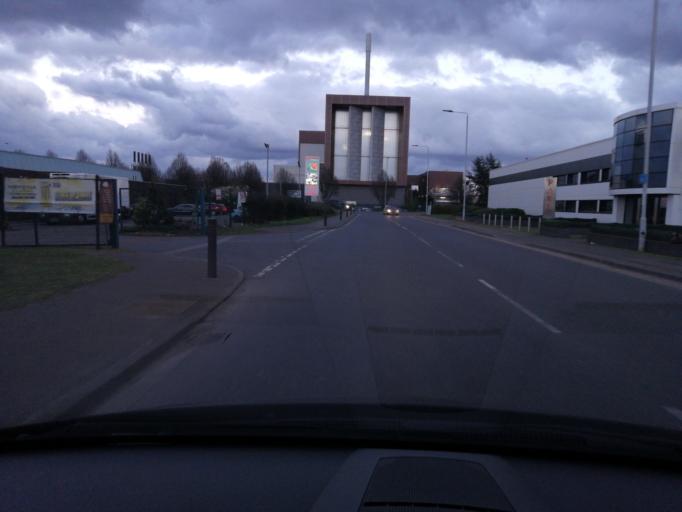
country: GB
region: England
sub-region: Peterborough
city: Eye
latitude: 52.5762
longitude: -0.2090
